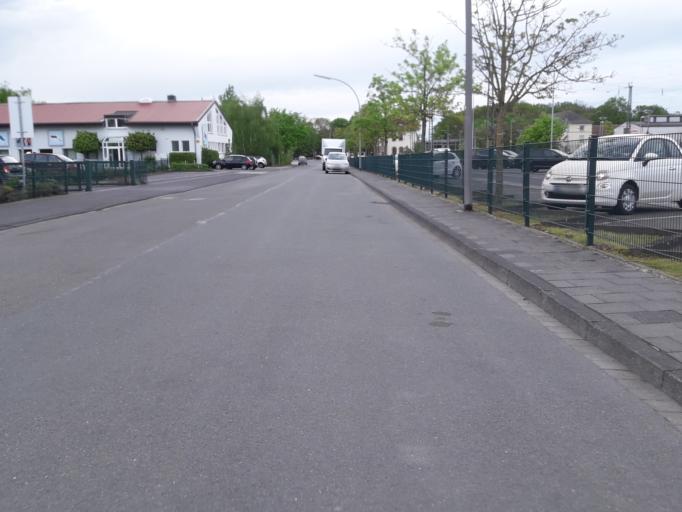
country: DE
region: North Rhine-Westphalia
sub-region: Regierungsbezirk Munster
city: Muenster
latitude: 51.9025
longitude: 7.6548
